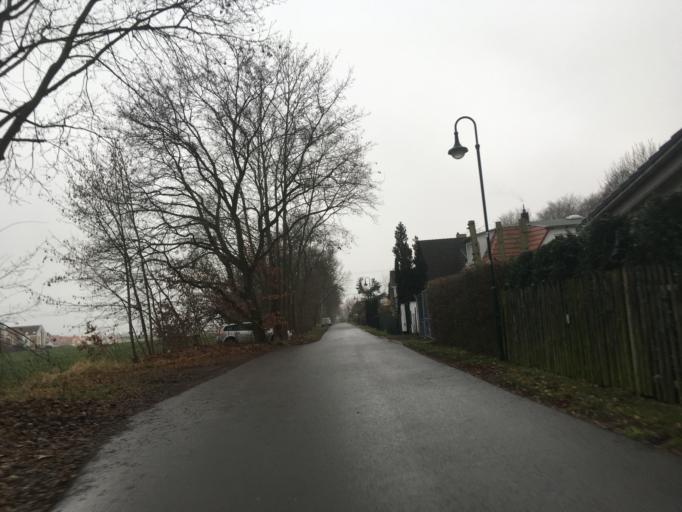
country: DE
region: Berlin
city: Buch
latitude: 52.6244
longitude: 13.5062
